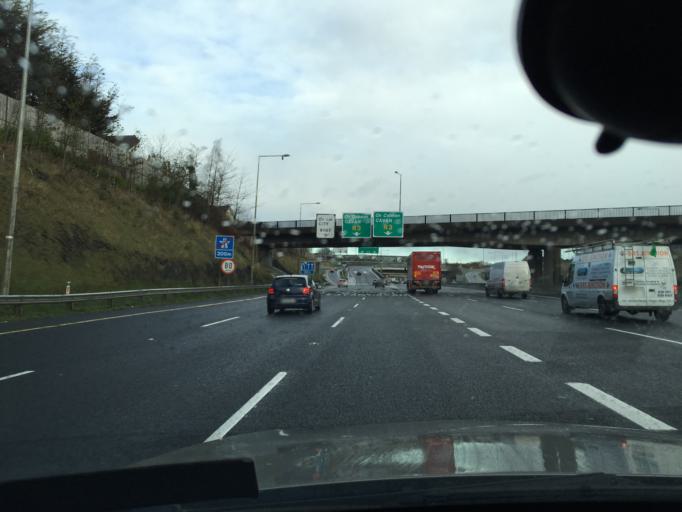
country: IE
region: Leinster
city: Castleknock
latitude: 53.3785
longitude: -6.3679
